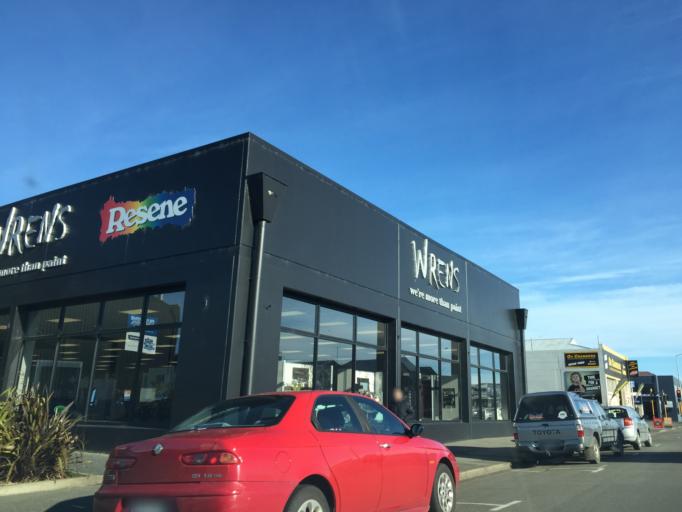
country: NZ
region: Southland
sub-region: Invercargill City
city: Invercargill
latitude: -46.4086
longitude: 168.3519
